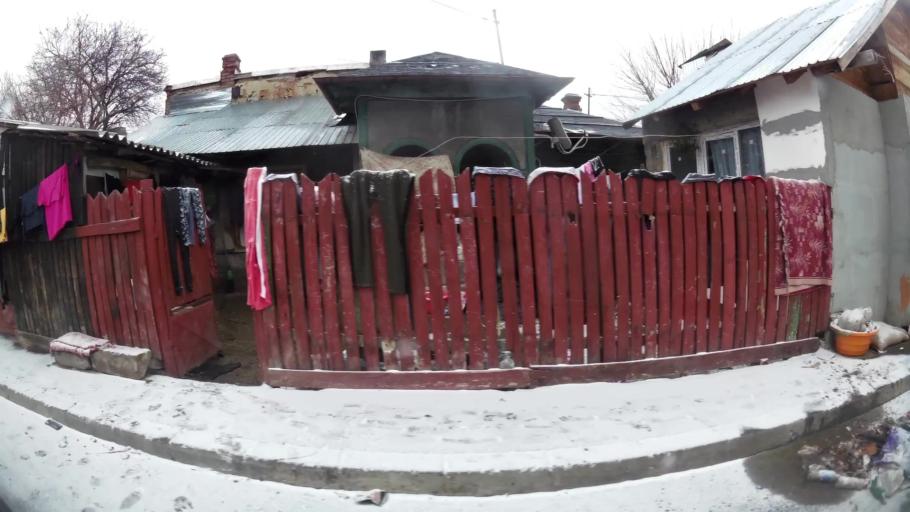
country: RO
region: Prahova
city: Ploiesti
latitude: 44.9529
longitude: 26.0151
